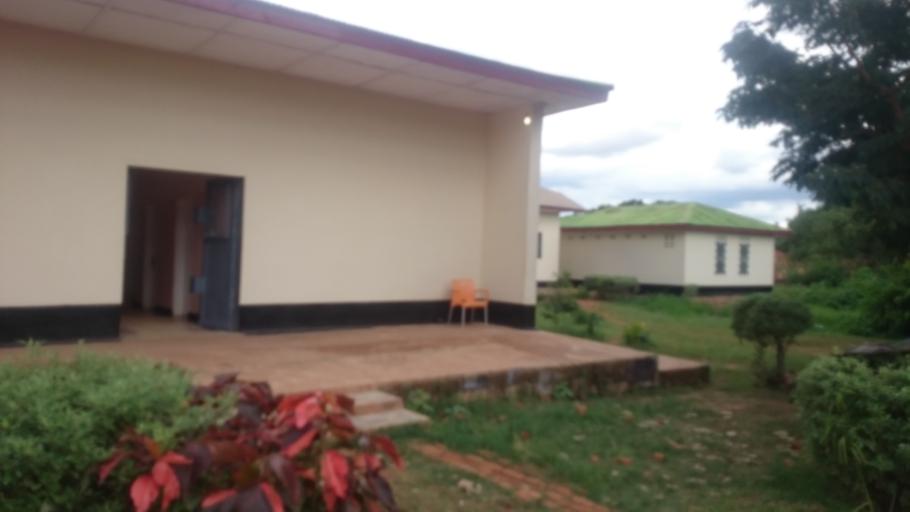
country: CD
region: Katanga
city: Lubumbashi
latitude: -11.6311
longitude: 27.4851
